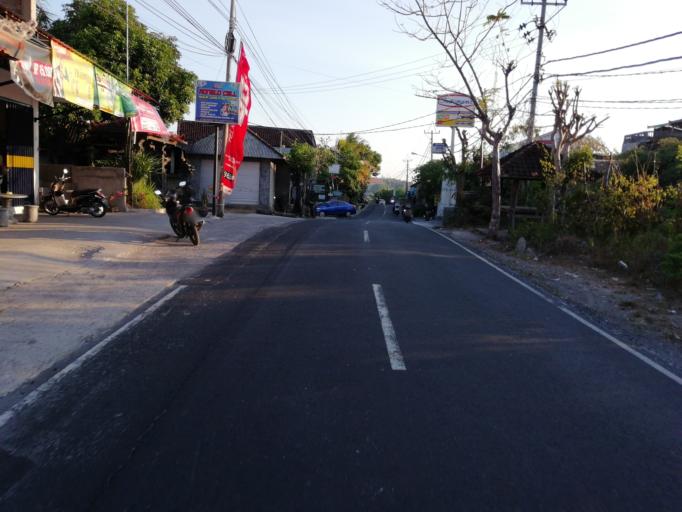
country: ID
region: Bali
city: Bualu
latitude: -8.8196
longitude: 115.1896
